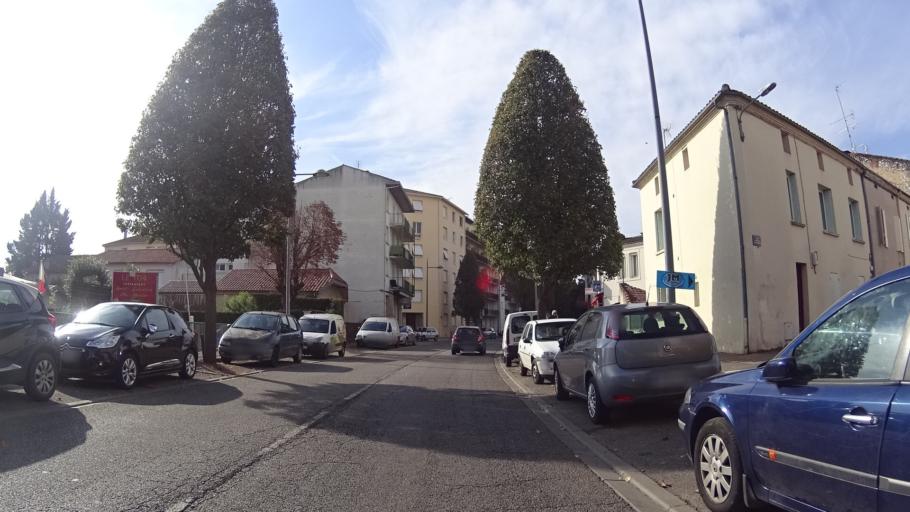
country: FR
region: Aquitaine
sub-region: Departement du Lot-et-Garonne
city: Agen
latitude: 44.1968
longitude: 0.6197
